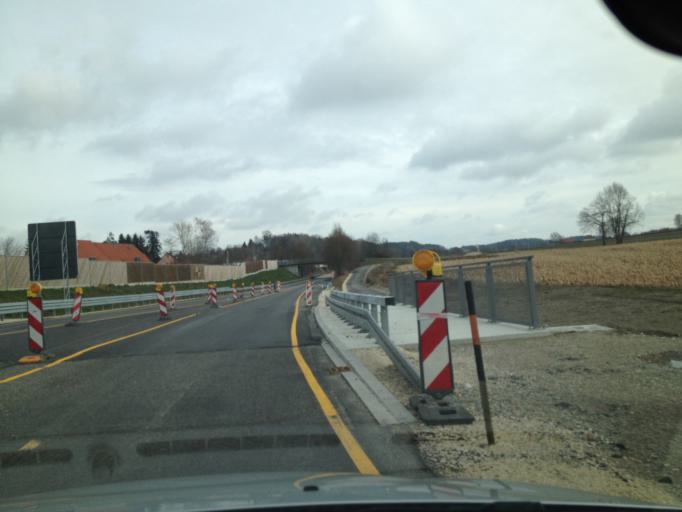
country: DE
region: Bavaria
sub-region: Swabia
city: Wertingen
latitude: 48.5533
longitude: 10.6897
